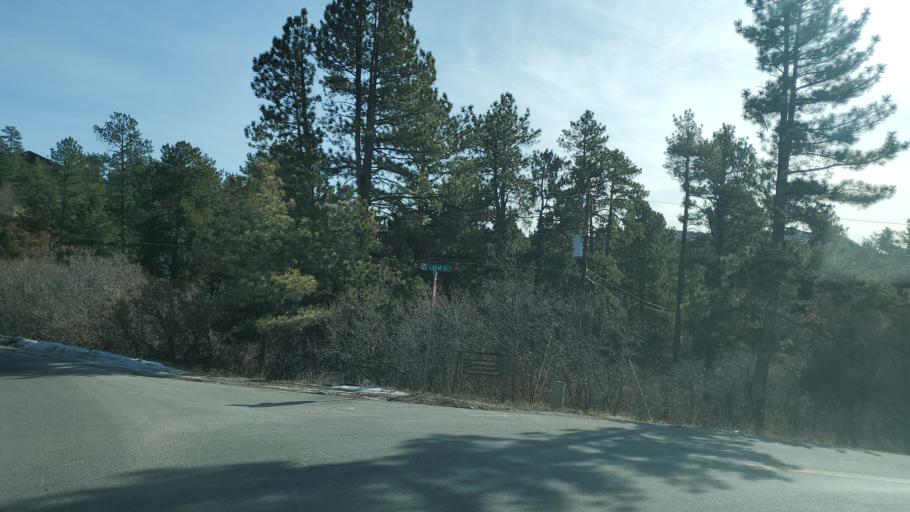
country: US
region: Colorado
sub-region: Douglas County
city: Castle Pines
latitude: 39.4366
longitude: -104.8747
